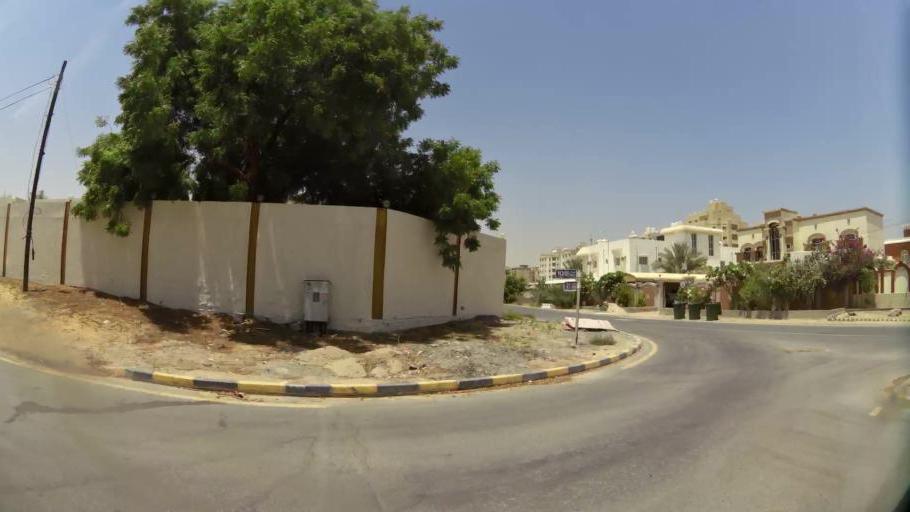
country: AE
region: Ajman
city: Ajman
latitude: 25.4078
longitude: 55.5169
